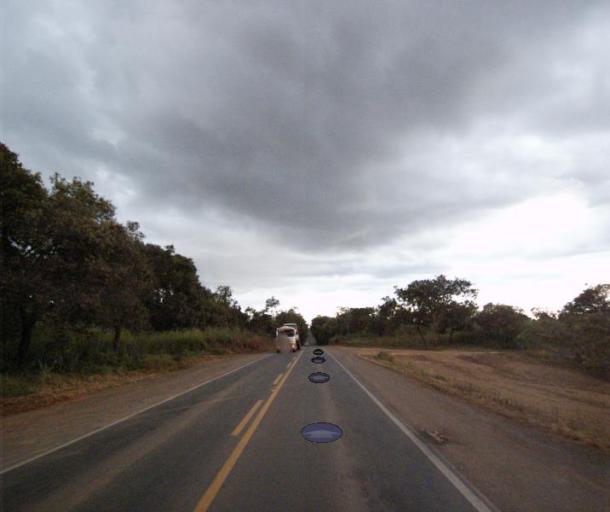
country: BR
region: Goias
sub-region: Uruacu
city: Uruacu
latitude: -14.6722
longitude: -49.2003
